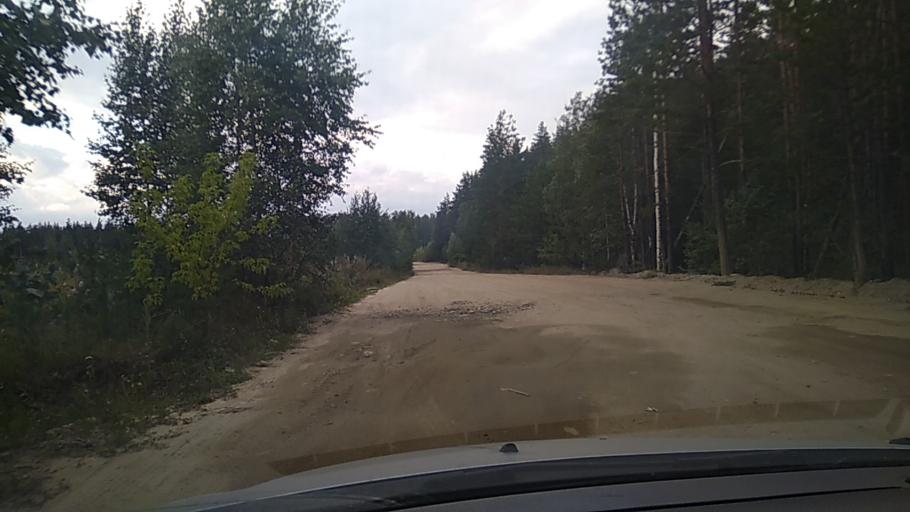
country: RU
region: Chelyabinsk
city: Kyshtym
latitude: 55.6816
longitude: 60.5728
